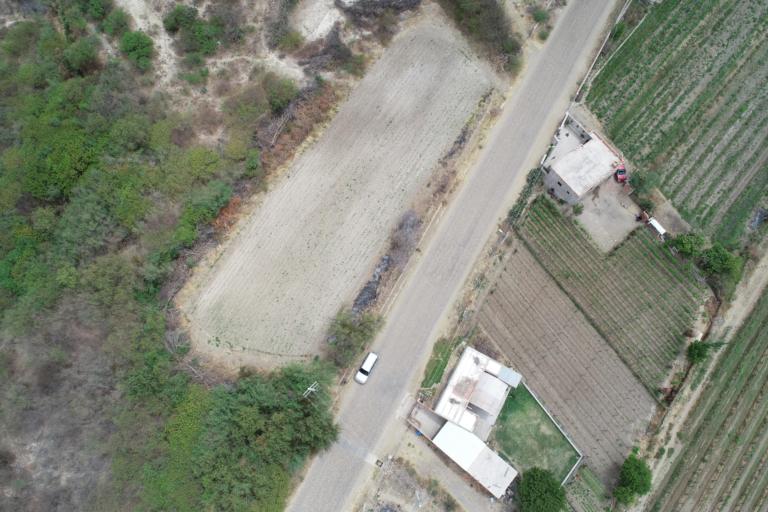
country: BO
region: Tarija
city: Tarija
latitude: -21.5951
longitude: -64.6253
